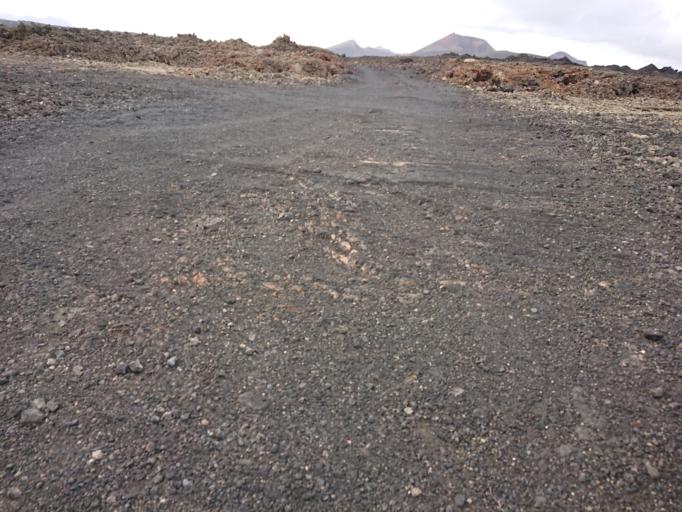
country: ES
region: Canary Islands
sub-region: Provincia de Las Palmas
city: Tias
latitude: 29.0018
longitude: -13.6882
